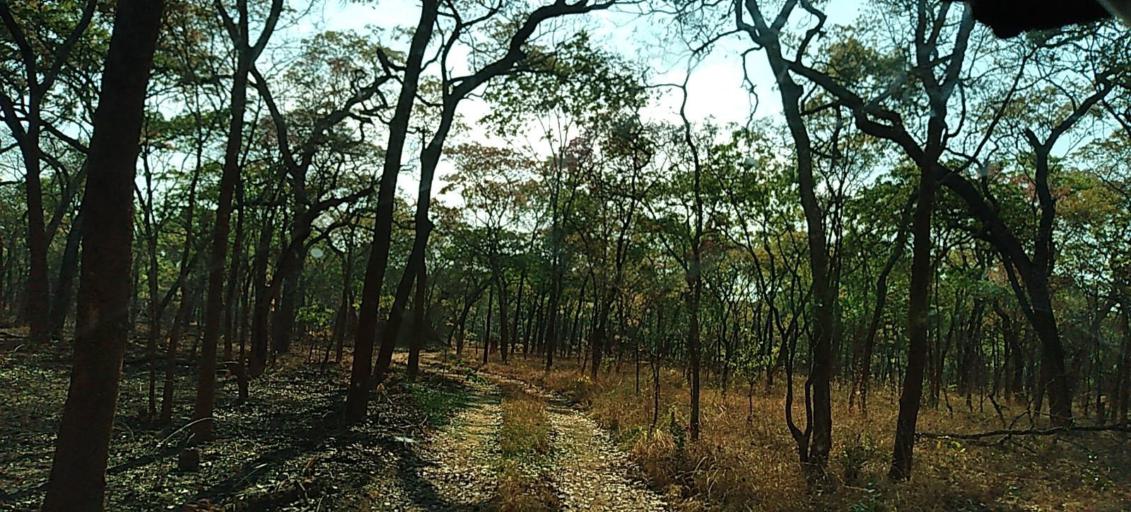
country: ZM
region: North-Western
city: Kalengwa
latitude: -13.2253
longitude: 25.0972
